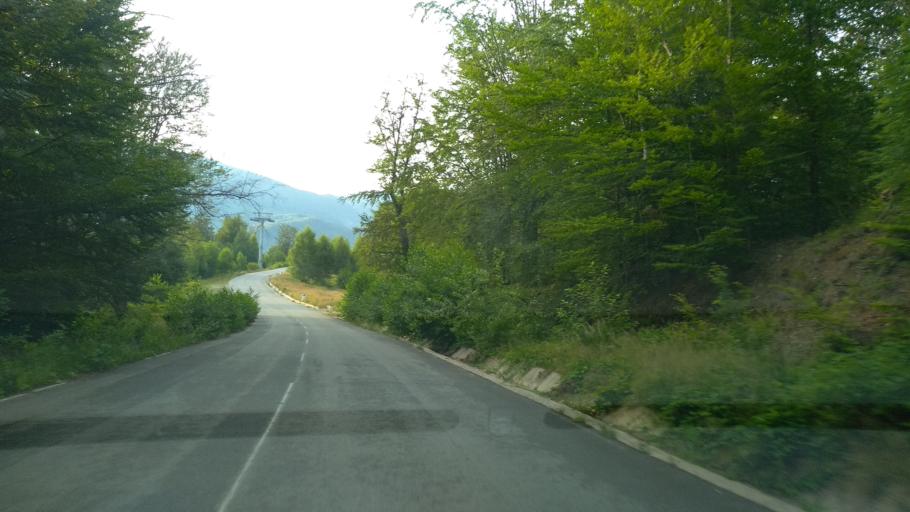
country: RO
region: Hunedoara
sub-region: Municipiul  Vulcan
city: Jiu-Paroseni
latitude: 45.3475
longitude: 23.2912
